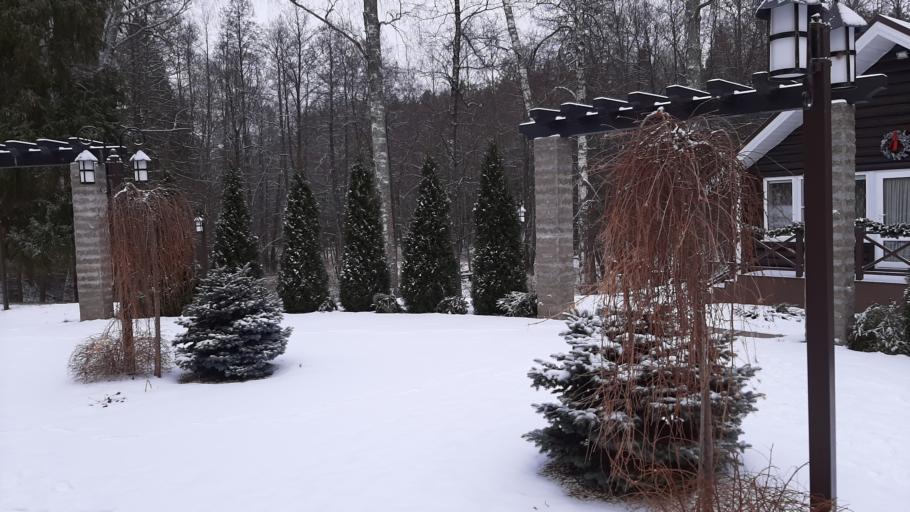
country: RU
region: Ivanovo
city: Kokhma
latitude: 56.8999
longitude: 41.0098
